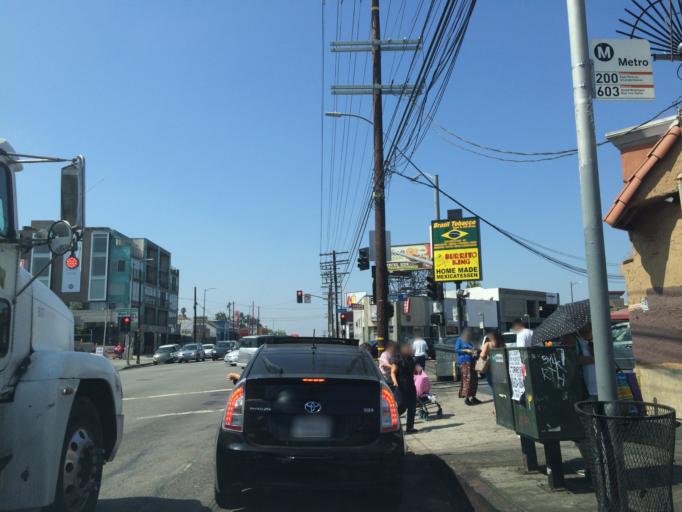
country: US
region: California
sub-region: Los Angeles County
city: Echo Park
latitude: 34.0779
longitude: -118.2634
